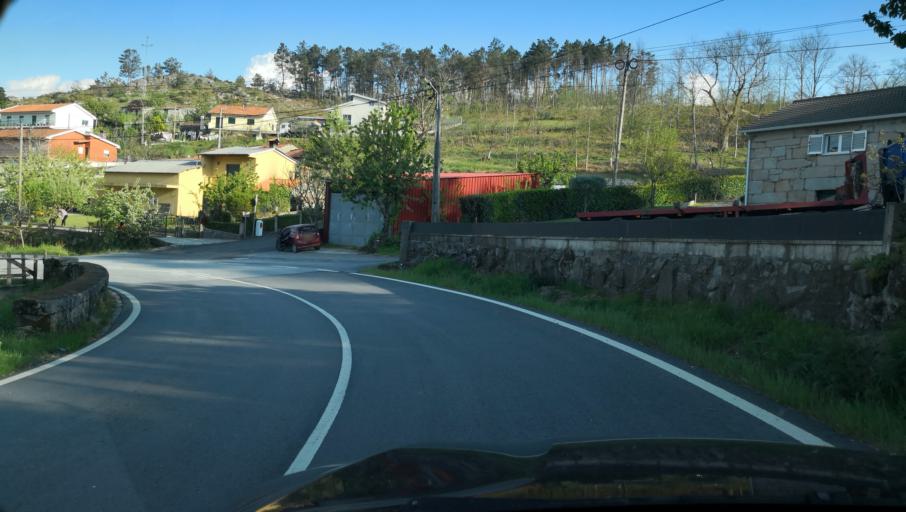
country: PT
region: Vila Real
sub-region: Santa Marta de Penaguiao
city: Santa Marta de Penaguiao
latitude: 41.2820
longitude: -7.8190
